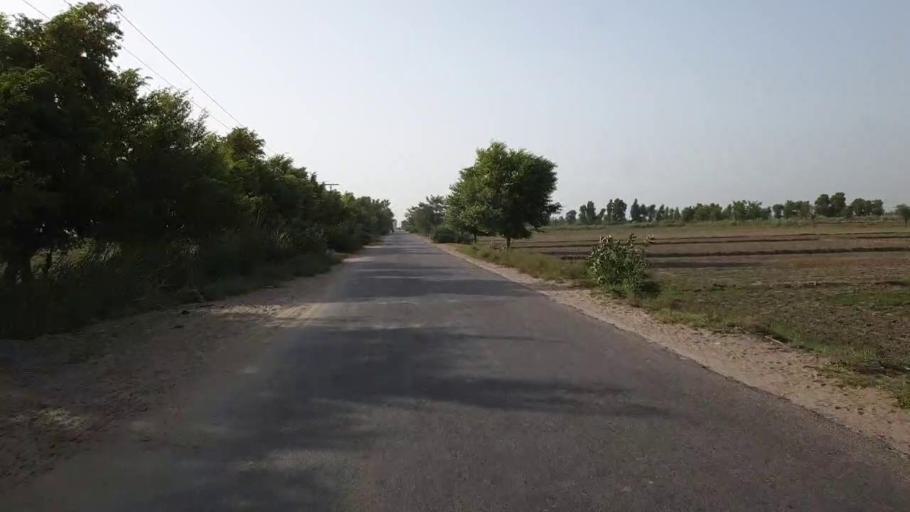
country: PK
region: Sindh
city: Jam Sahib
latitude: 26.3881
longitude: 68.8823
